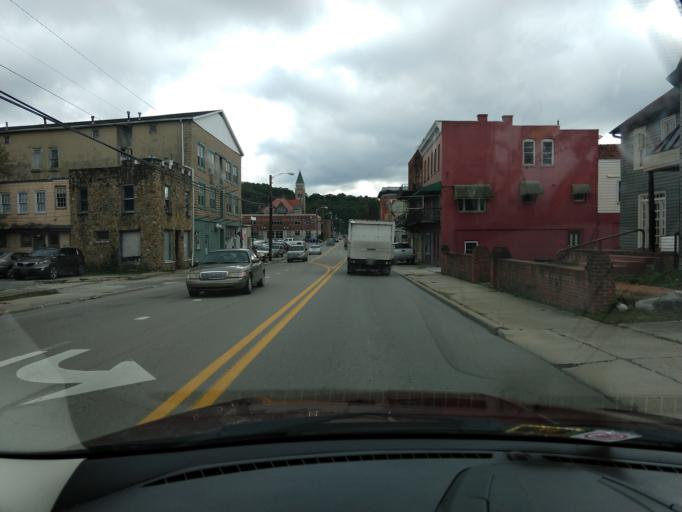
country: US
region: West Virginia
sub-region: Randolph County
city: Elkins
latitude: 38.9247
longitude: -79.8452
